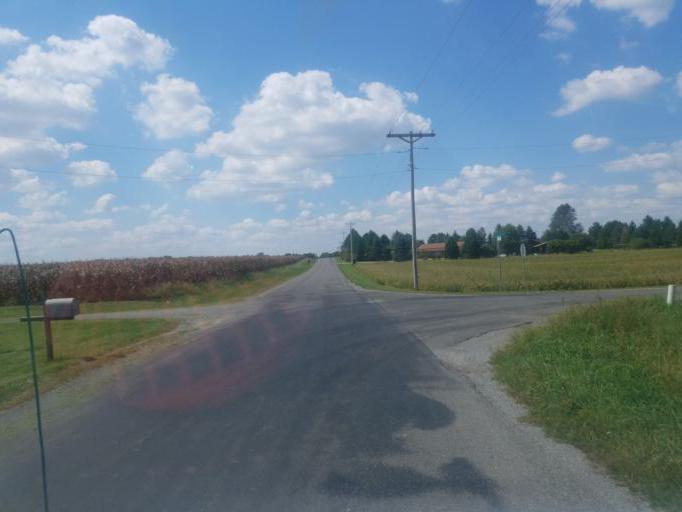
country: US
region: Ohio
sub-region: Hardin County
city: Ada
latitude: 40.6523
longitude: -83.8799
